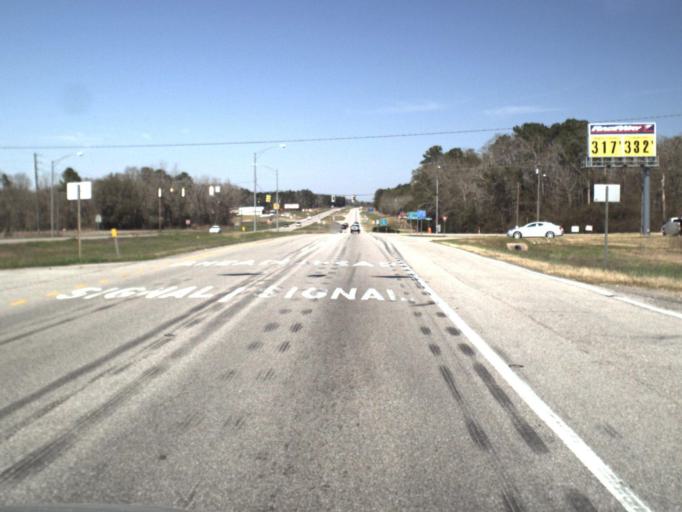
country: US
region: Alabama
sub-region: Houston County
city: Cottonwood
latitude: 30.9983
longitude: -85.4075
